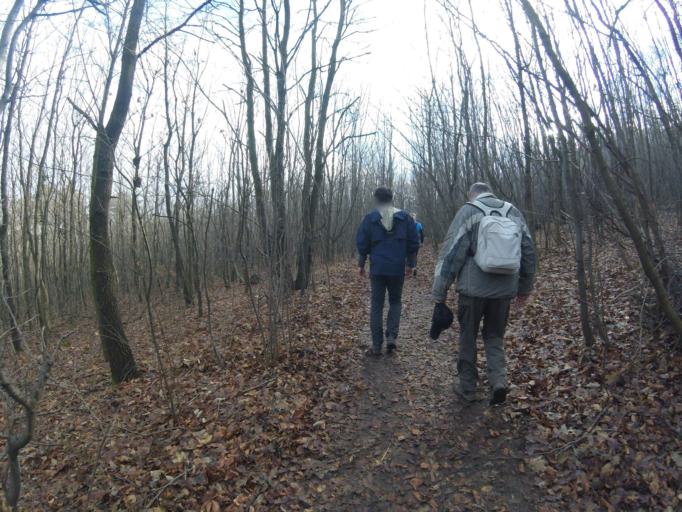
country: HU
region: Pest
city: Budakeszi
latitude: 47.5203
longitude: 18.9662
